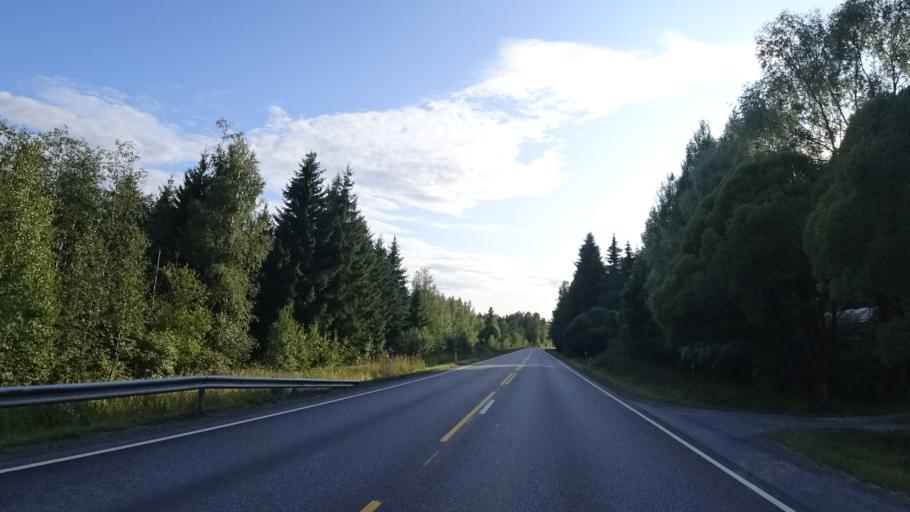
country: FI
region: South Karelia
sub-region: Imatra
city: Parikkala
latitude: 61.6114
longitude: 29.5138
